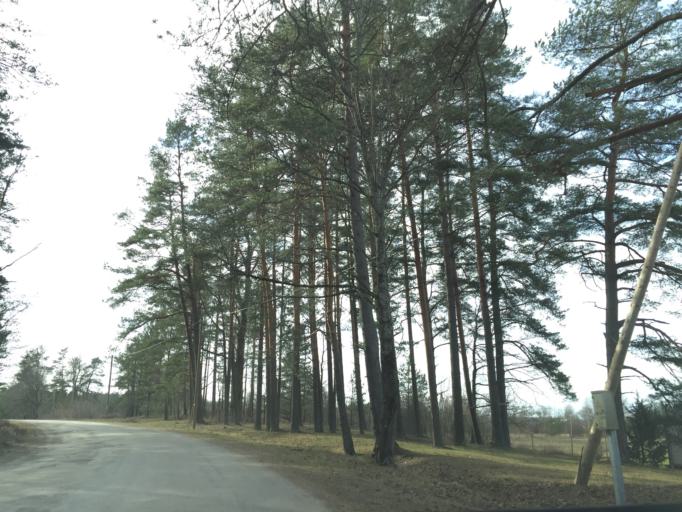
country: LV
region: Garkalne
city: Garkalne
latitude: 57.0690
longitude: 24.4167
